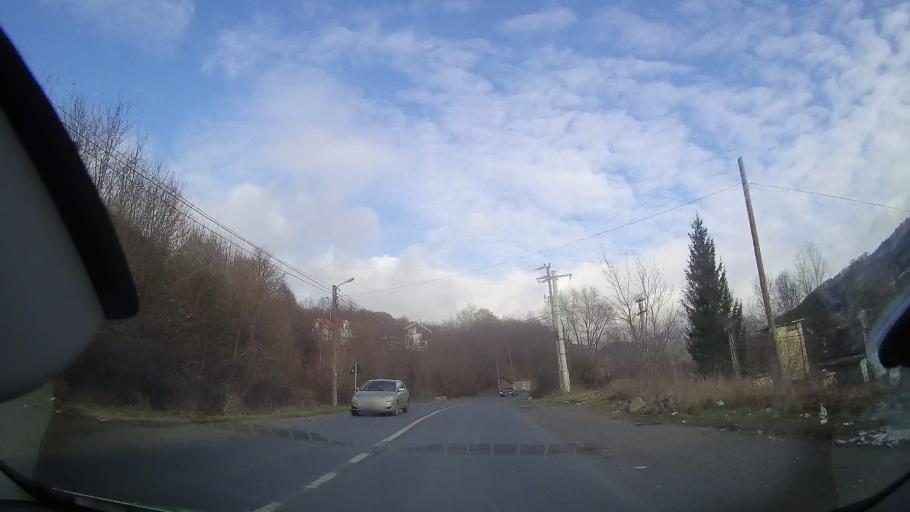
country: RO
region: Alba
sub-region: Comuna Bistra
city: Bistra
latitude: 46.3632
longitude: 23.0806
